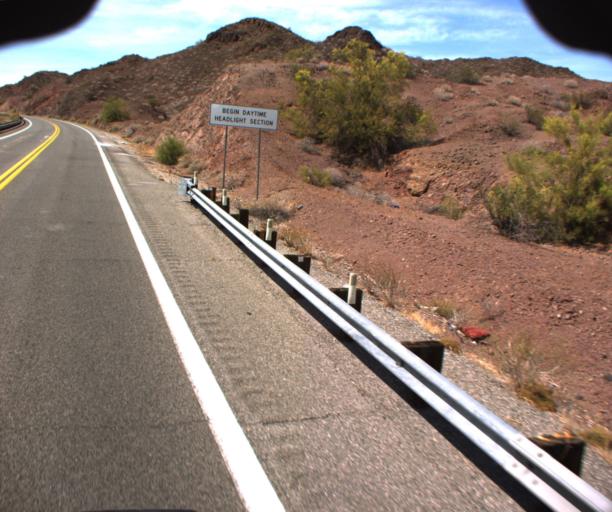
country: US
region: Arizona
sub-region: La Paz County
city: Cienega Springs
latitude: 34.3071
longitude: -114.0991
